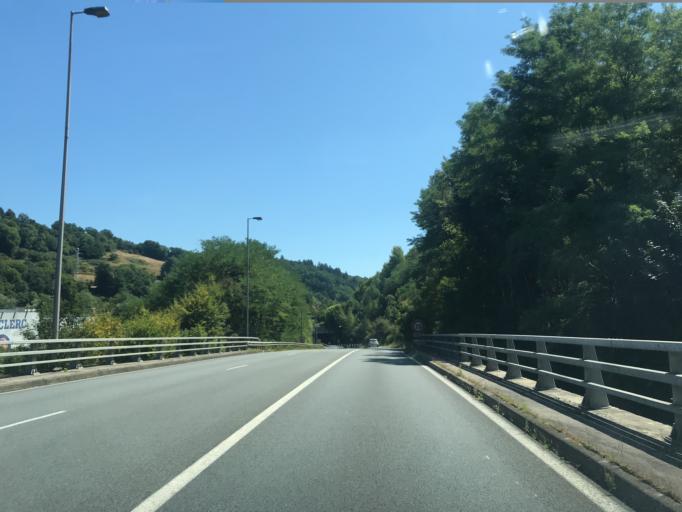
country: FR
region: Limousin
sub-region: Departement de la Correze
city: Tulle
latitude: 45.2519
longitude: 1.7598
